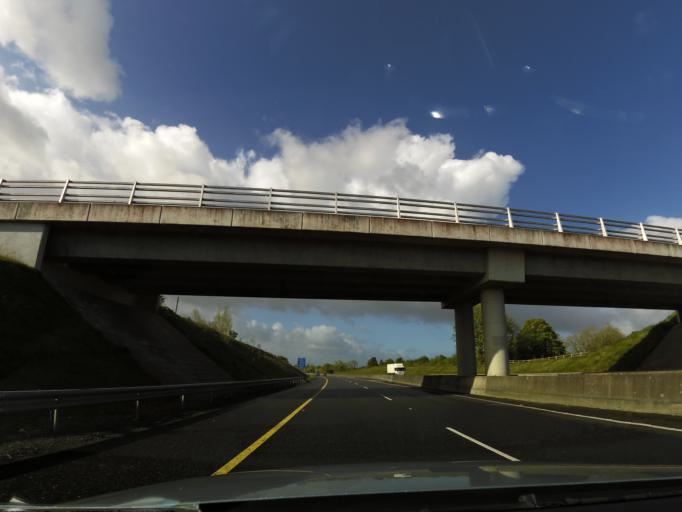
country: IE
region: Munster
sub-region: County Limerick
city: Castleconnell
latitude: 52.6952
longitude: -8.4952
